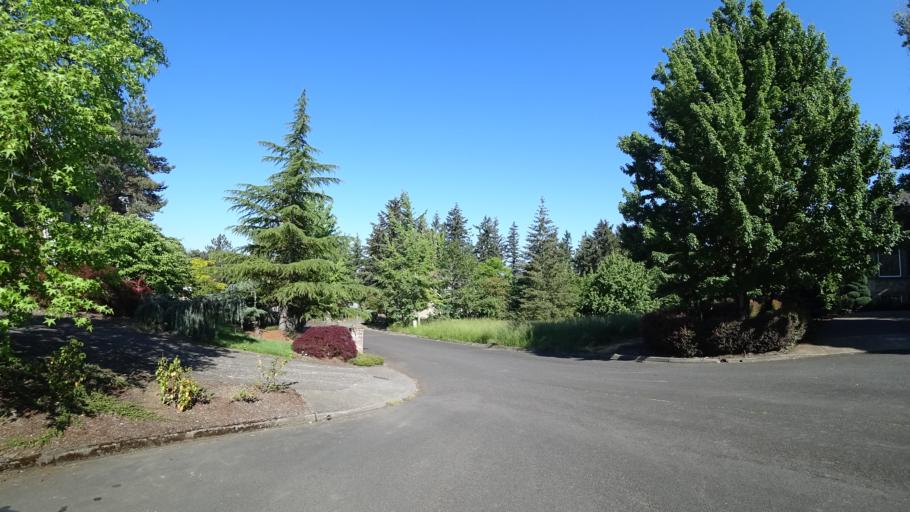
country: US
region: Oregon
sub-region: Clackamas County
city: Happy Valley
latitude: 45.4668
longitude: -122.5430
